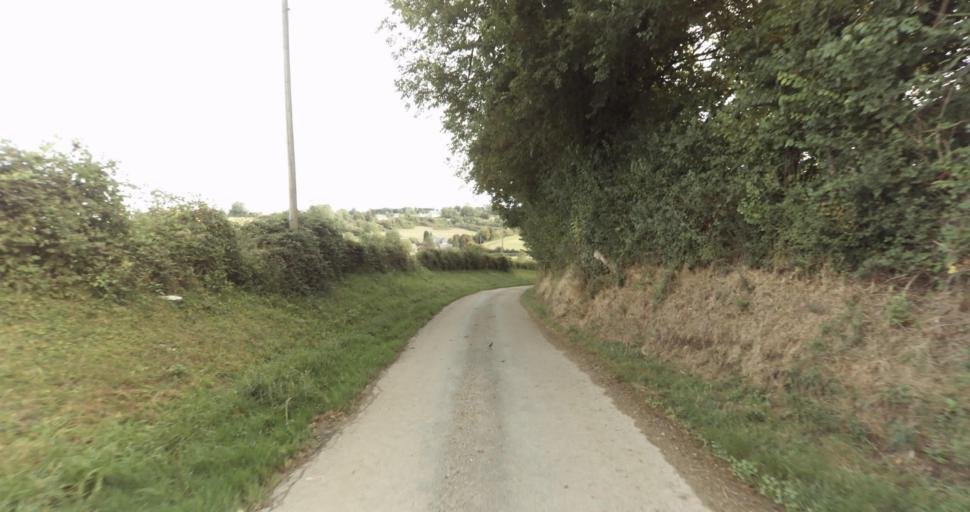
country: FR
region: Lower Normandy
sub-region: Departement de l'Orne
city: Vimoutiers
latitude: 48.8728
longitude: 0.2322
